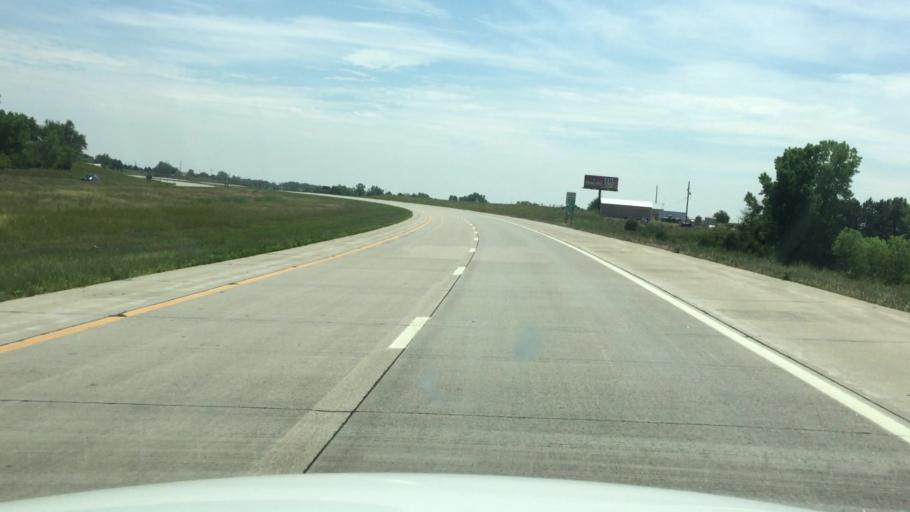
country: US
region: Kansas
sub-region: Jackson County
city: Holton
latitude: 39.3385
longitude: -95.7284
